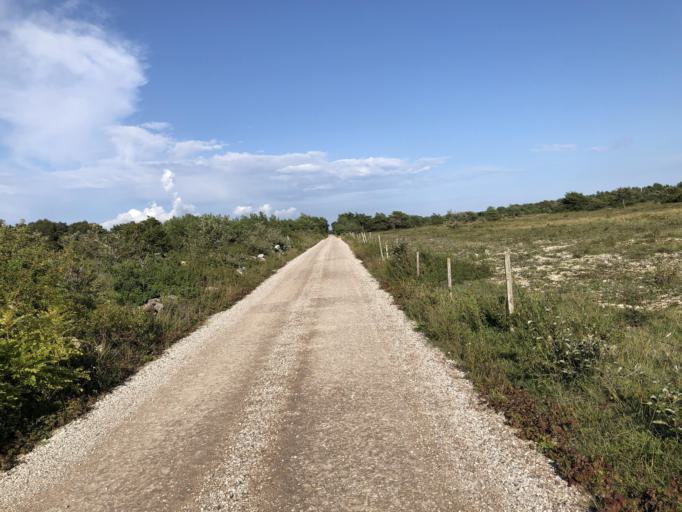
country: SE
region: Gotland
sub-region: Gotland
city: Hemse
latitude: 57.0300
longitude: 18.2478
